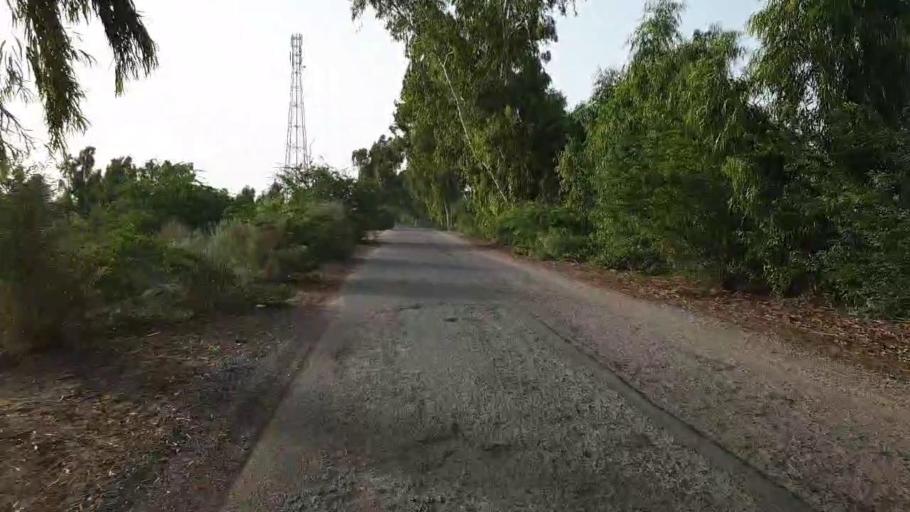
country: PK
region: Sindh
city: Bozdar
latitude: 27.1139
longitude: 68.9583
